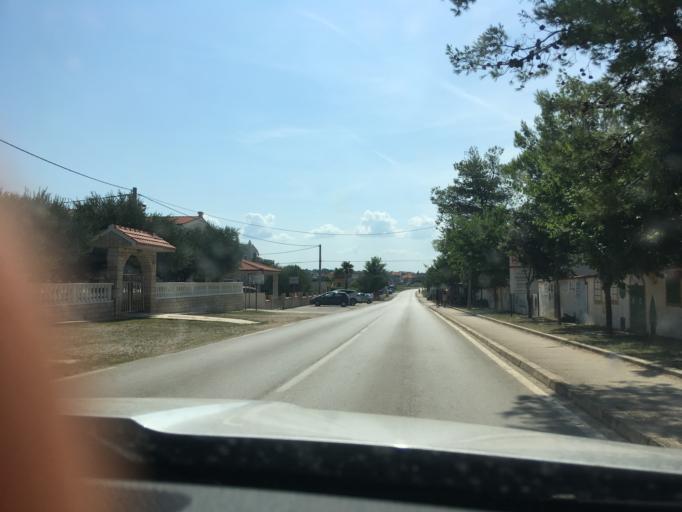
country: HR
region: Zadarska
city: Privlaka
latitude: 44.2566
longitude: 15.1265
